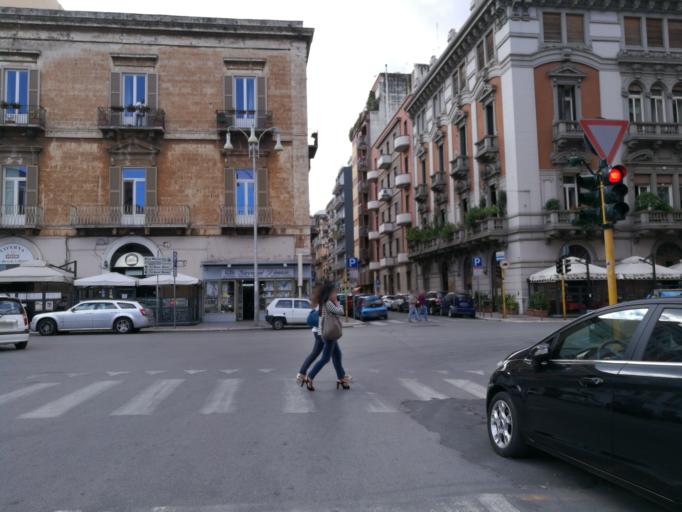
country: IT
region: Apulia
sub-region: Provincia di Bari
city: Bari
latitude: 41.1261
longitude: 16.8663
